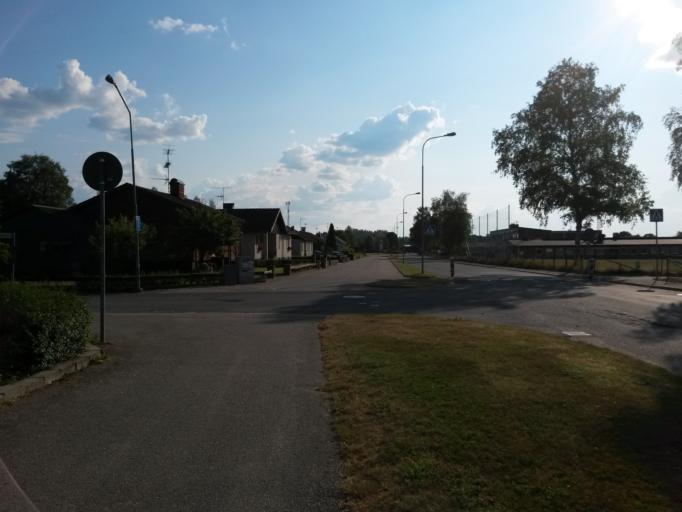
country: SE
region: Vaestra Goetaland
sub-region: Vargarda Kommun
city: Vargarda
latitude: 58.0334
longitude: 12.8214
